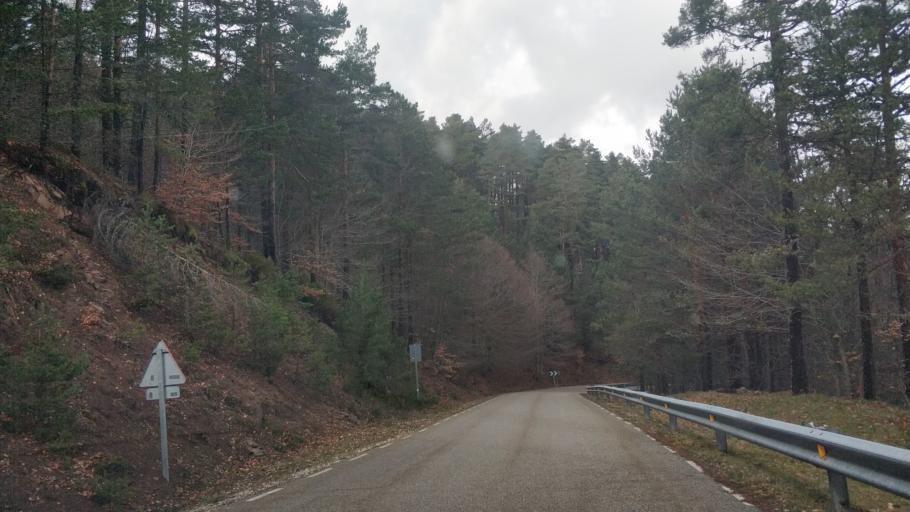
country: ES
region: Castille and Leon
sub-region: Provincia de Burgos
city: Neila
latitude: 42.0440
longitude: -3.0109
